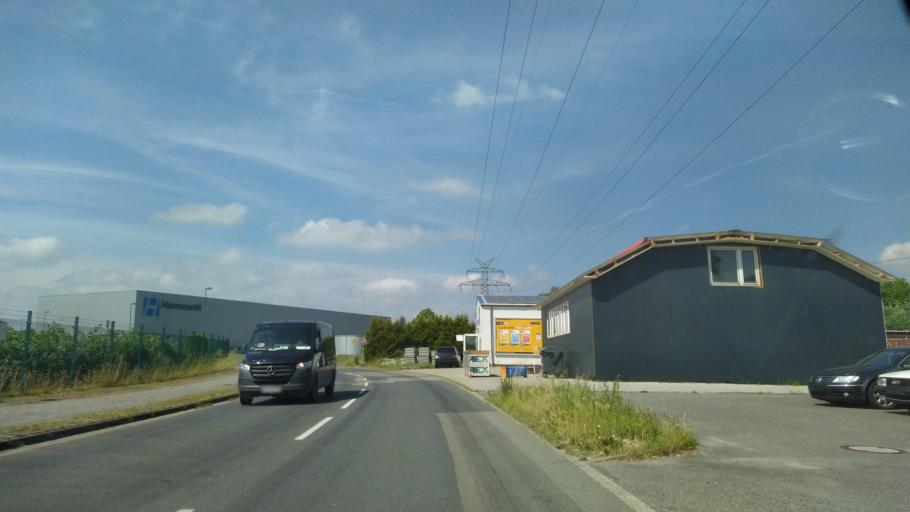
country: DE
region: Lower Saxony
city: Leer
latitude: 53.2188
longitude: 7.4642
